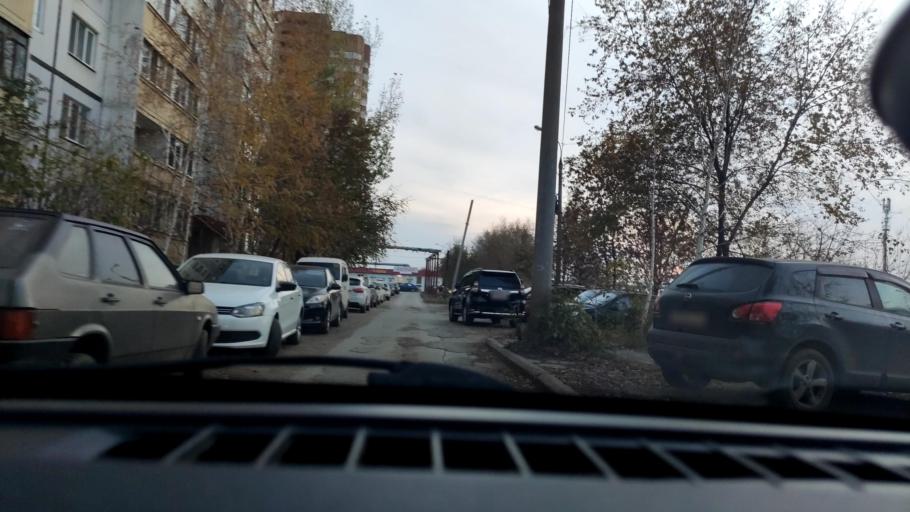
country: RU
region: Samara
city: Samara
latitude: 53.1082
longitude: 50.0813
